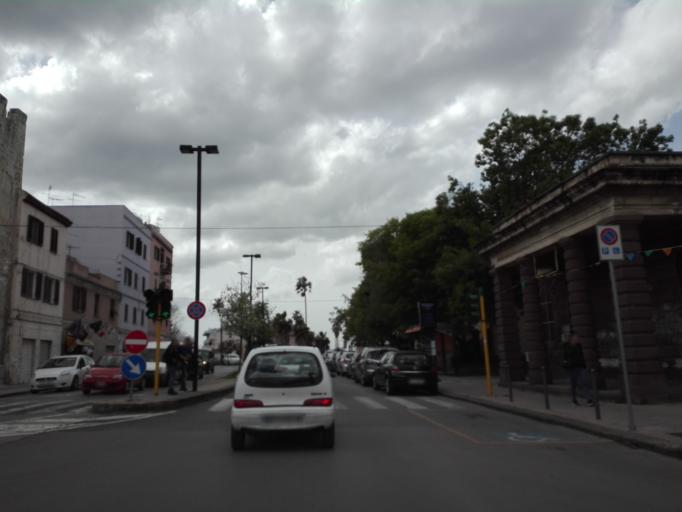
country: IT
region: Sardinia
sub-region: Provincia di Sassari
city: Sassari
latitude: 40.7303
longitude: 8.5560
